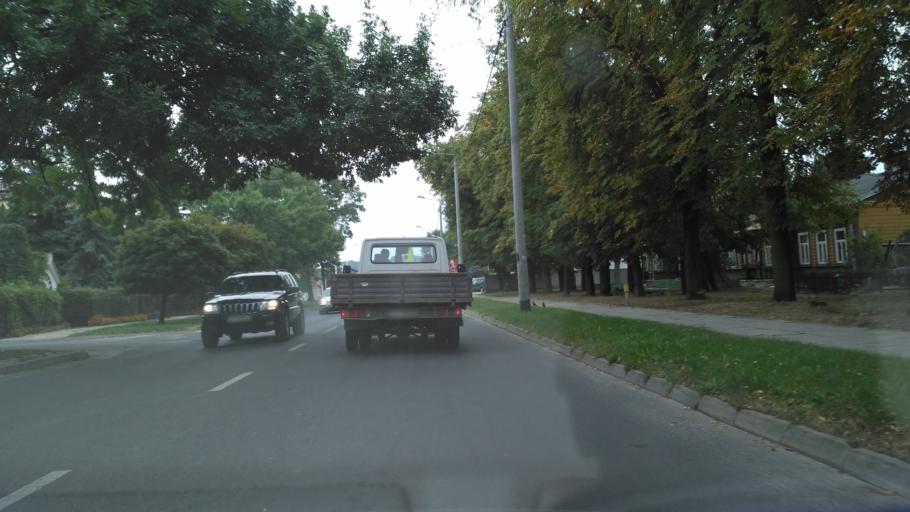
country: PL
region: Lublin Voivodeship
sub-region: Chelm
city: Chelm
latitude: 51.1409
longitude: 23.4525
